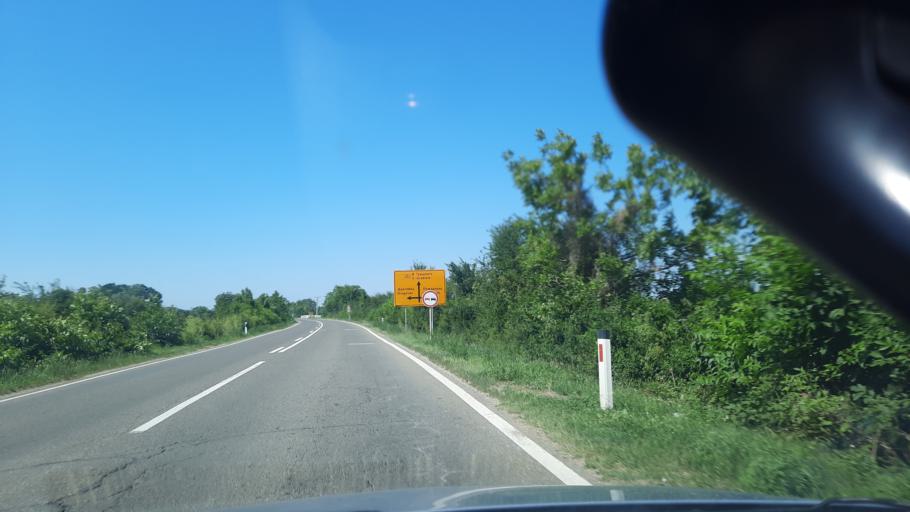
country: RS
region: Central Serbia
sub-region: Branicevski Okrug
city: Pozarevac
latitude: 44.6183
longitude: 21.1461
